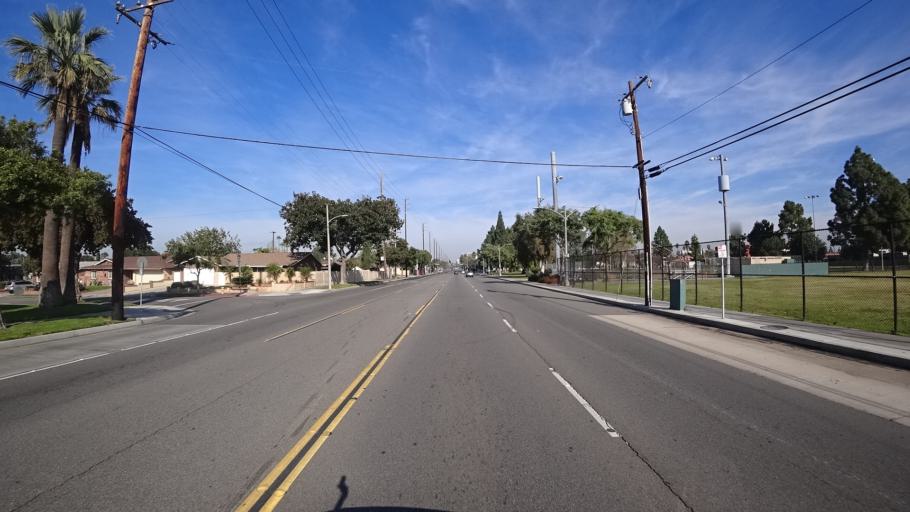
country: US
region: California
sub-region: Orange County
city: Garden Grove
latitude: 33.7941
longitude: -117.9063
